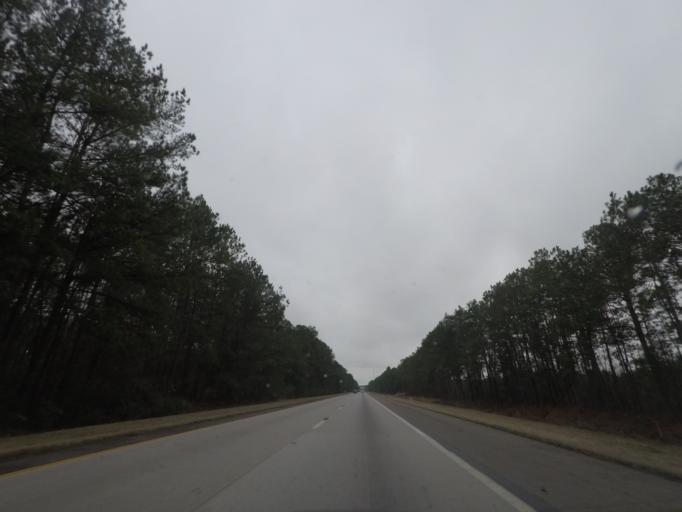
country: US
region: South Carolina
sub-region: Dorchester County
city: Saint George
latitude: 33.0626
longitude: -80.6632
